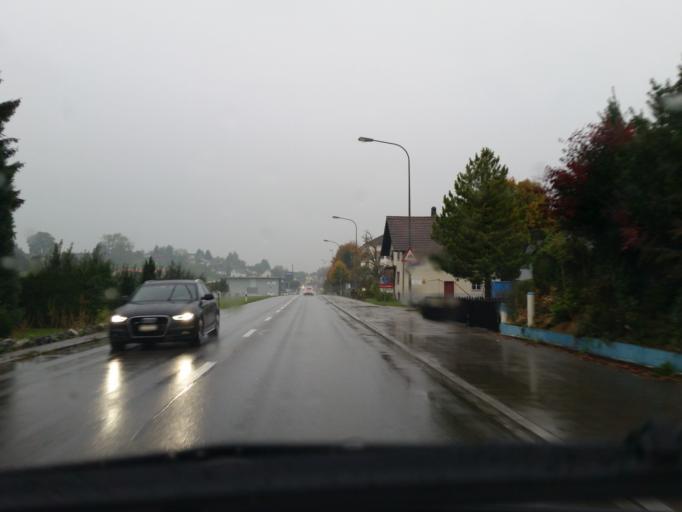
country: CH
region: Thurgau
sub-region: Weinfelden District
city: Erlen
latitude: 47.5471
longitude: 9.2266
